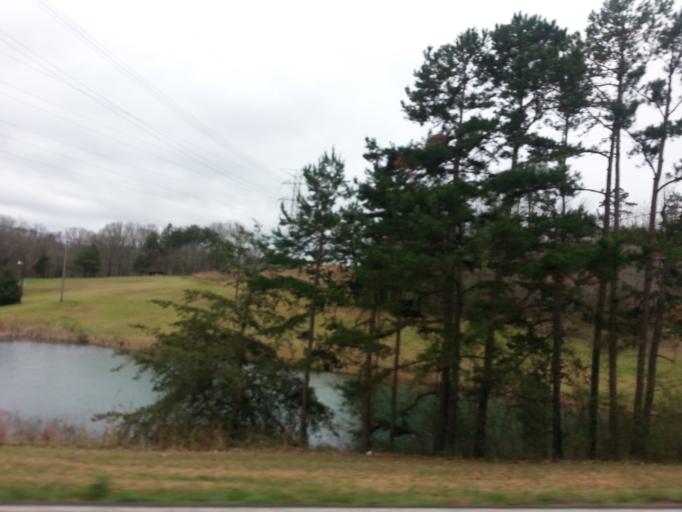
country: US
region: Tennessee
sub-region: Knox County
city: Knoxville
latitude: 35.9940
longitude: -84.0189
